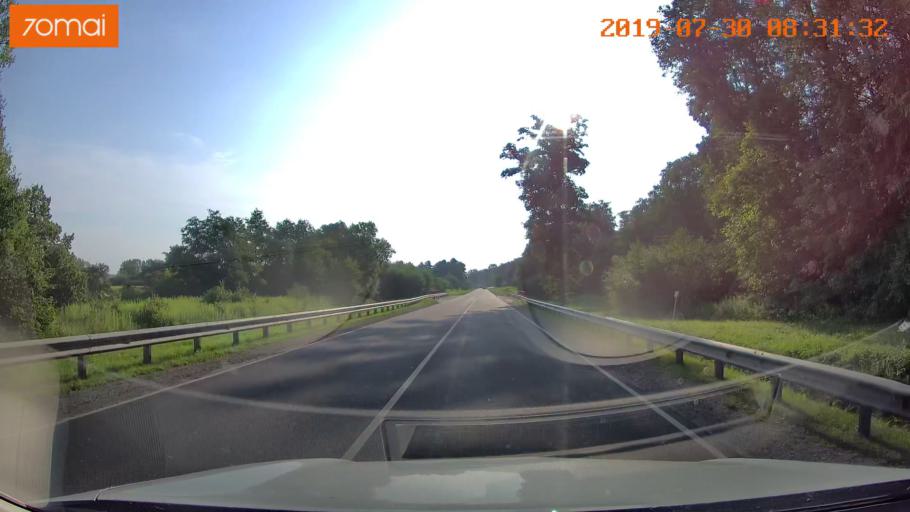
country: RU
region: Kaliningrad
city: Chernyakhovsk
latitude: 54.6380
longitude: 21.7093
